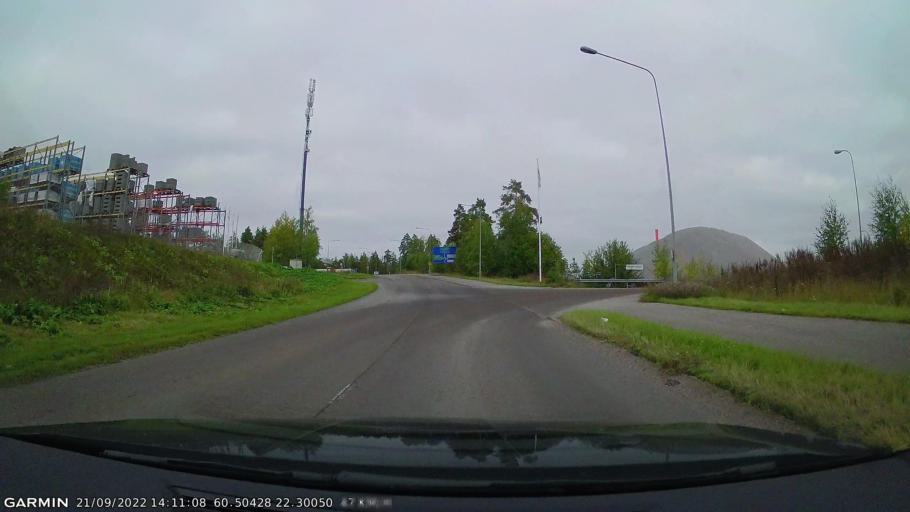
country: FI
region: Varsinais-Suomi
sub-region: Turku
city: Turku
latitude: 60.5042
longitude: 22.3013
